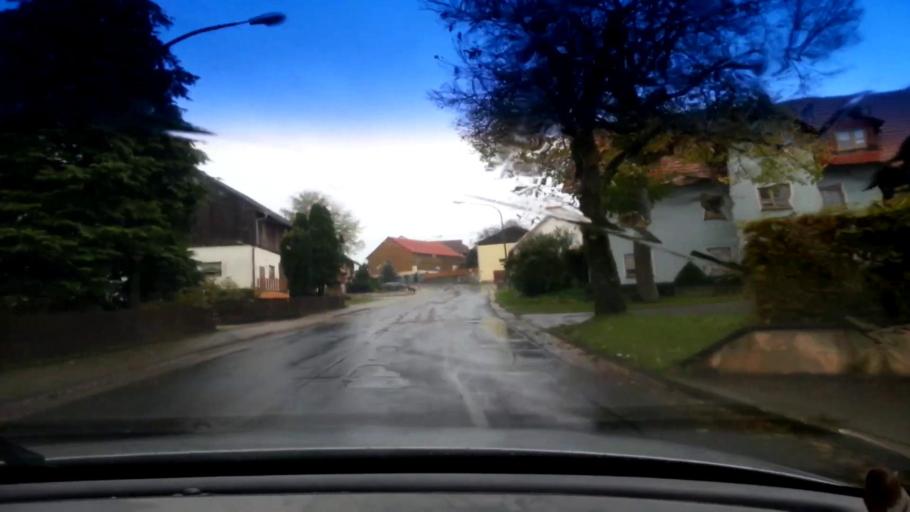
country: DE
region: Bavaria
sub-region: Upper Franconia
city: Wattendorf
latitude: 50.0366
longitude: 11.1525
